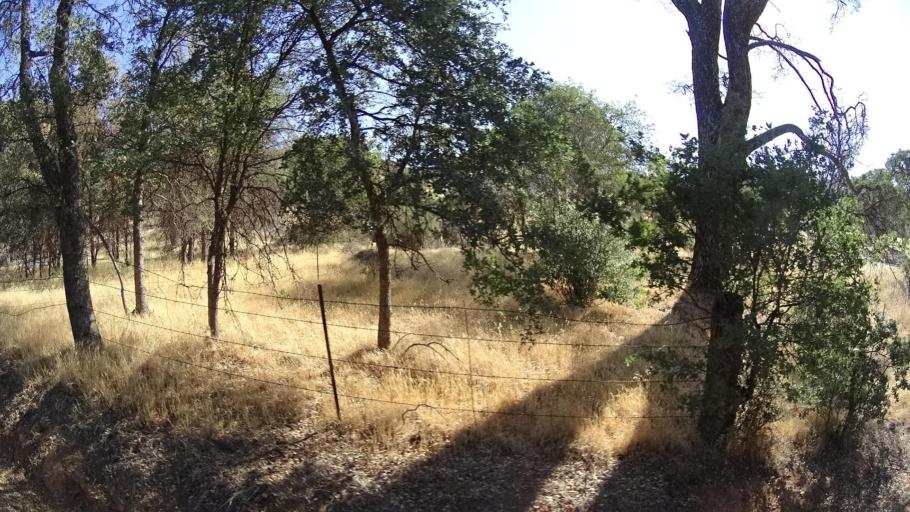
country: US
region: California
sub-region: Mariposa County
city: Mariposa
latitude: 37.6020
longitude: -120.1976
